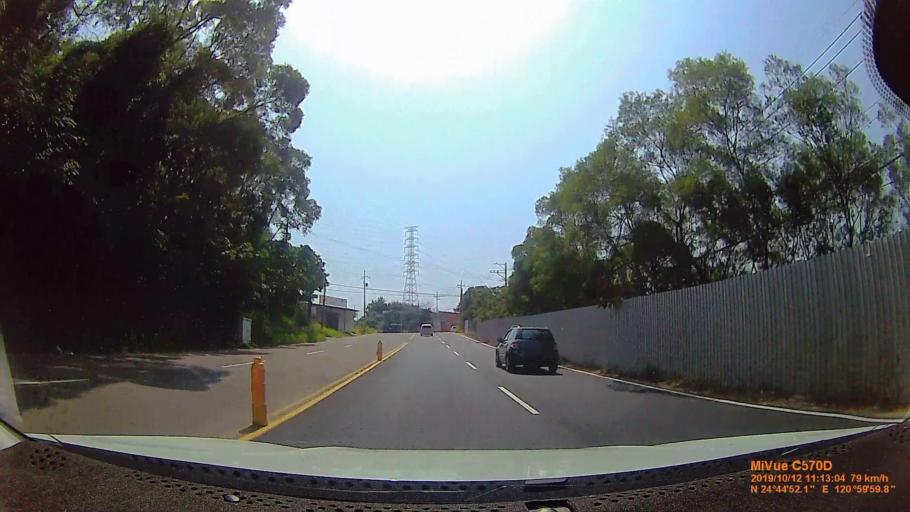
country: TW
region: Taiwan
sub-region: Hsinchu
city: Hsinchu
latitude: 24.7476
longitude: 121.0000
